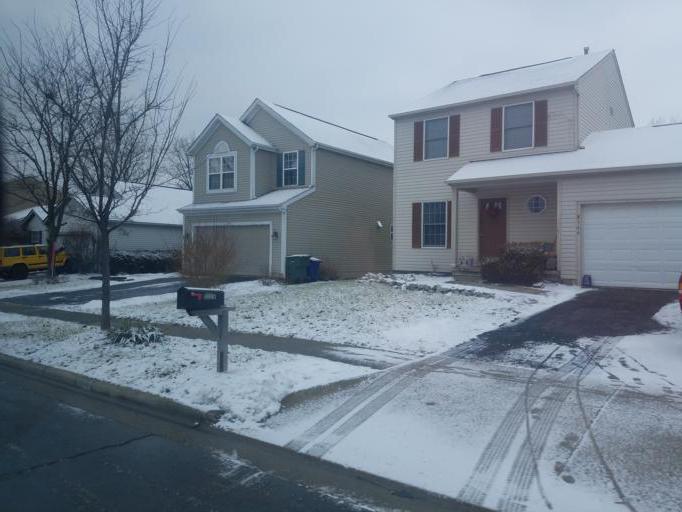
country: US
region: Ohio
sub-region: Franklin County
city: Reynoldsburg
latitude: 39.9978
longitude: -82.7811
